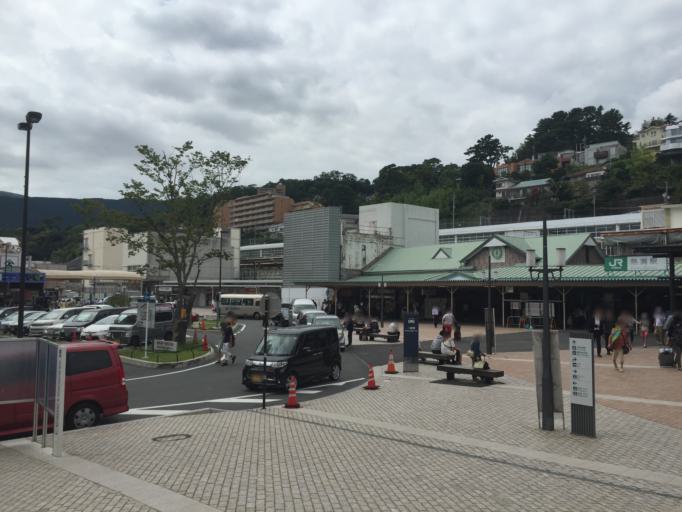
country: JP
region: Shizuoka
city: Atami
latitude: 35.1035
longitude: 139.0786
